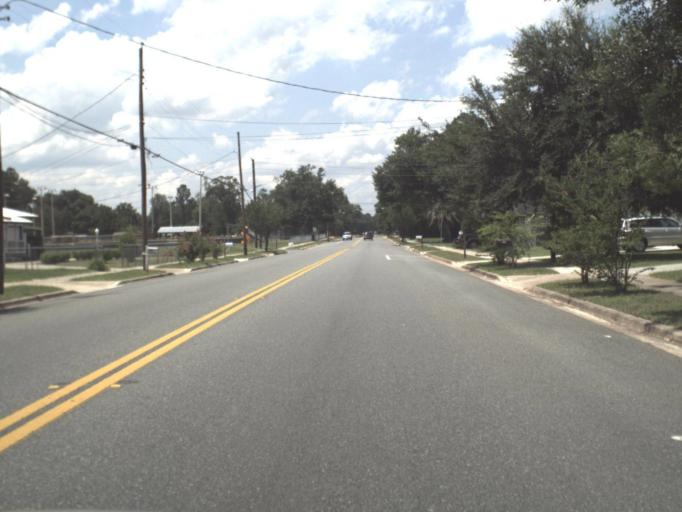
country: US
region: Florida
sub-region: Baker County
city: Macclenny
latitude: 30.2864
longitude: -82.1246
